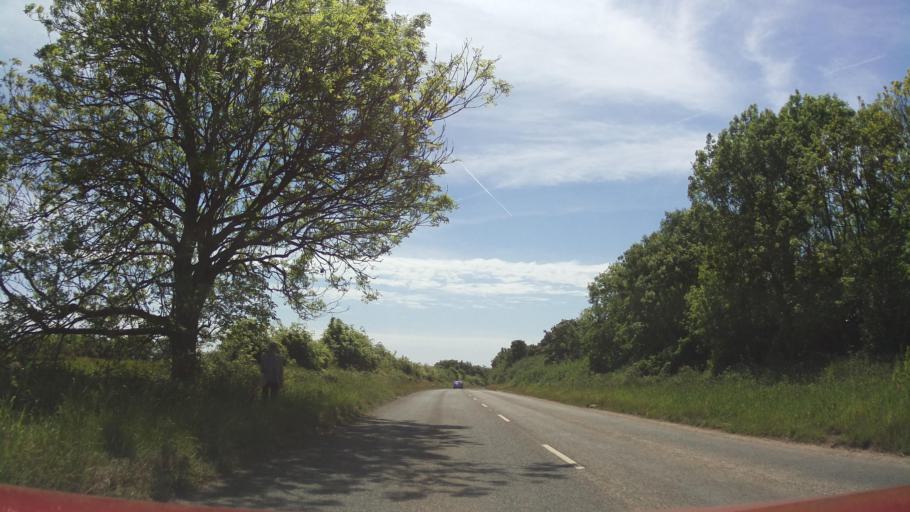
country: GB
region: England
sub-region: Devon
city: Budleigh Salterton
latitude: 50.6438
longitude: -3.3170
